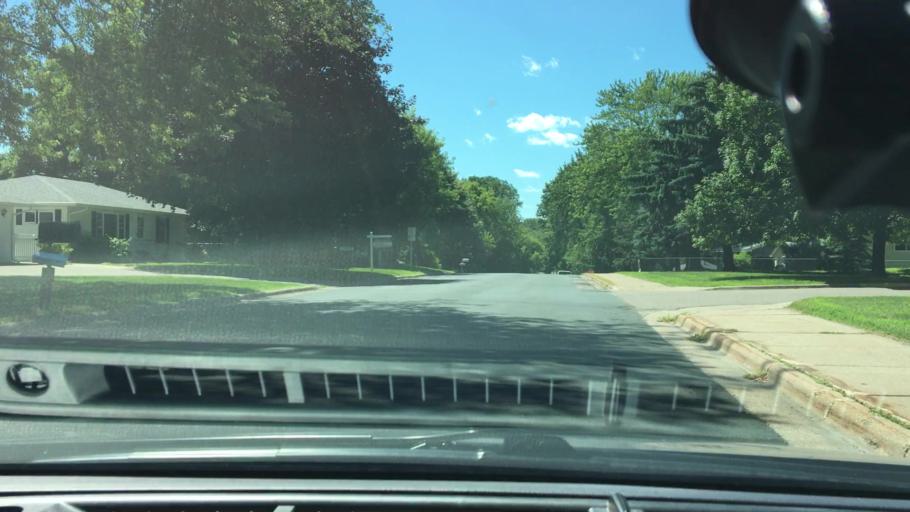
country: US
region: Minnesota
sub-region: Hennepin County
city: Maple Grove
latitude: 45.0693
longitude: -93.4525
